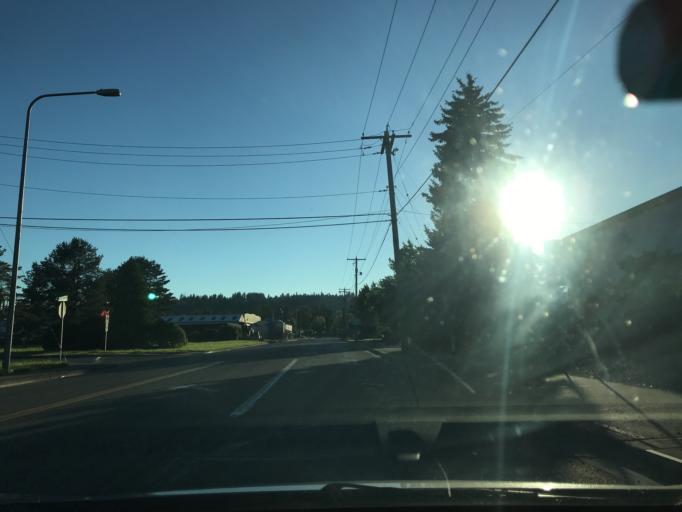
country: US
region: Washington
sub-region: Pierce County
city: Sumner
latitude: 47.2130
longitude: -122.2342
